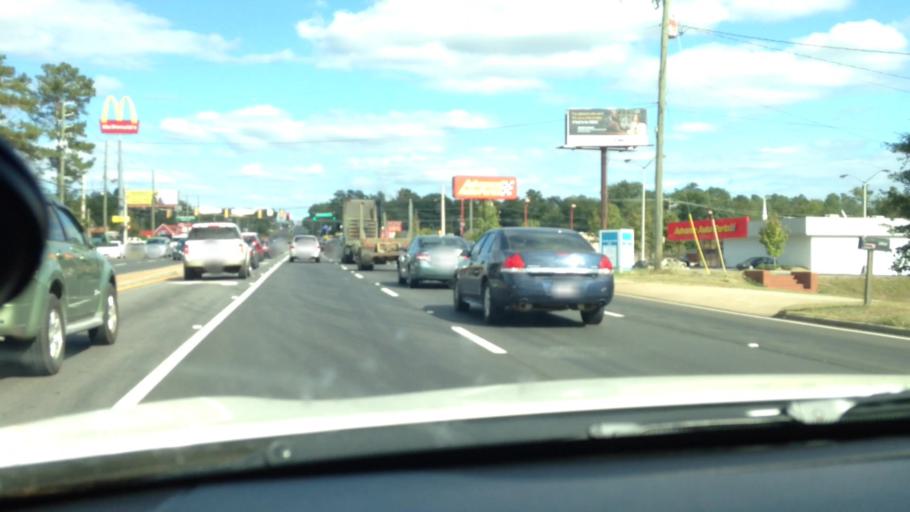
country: US
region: Georgia
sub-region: Columbia County
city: Martinez
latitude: 33.4186
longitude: -82.0806
